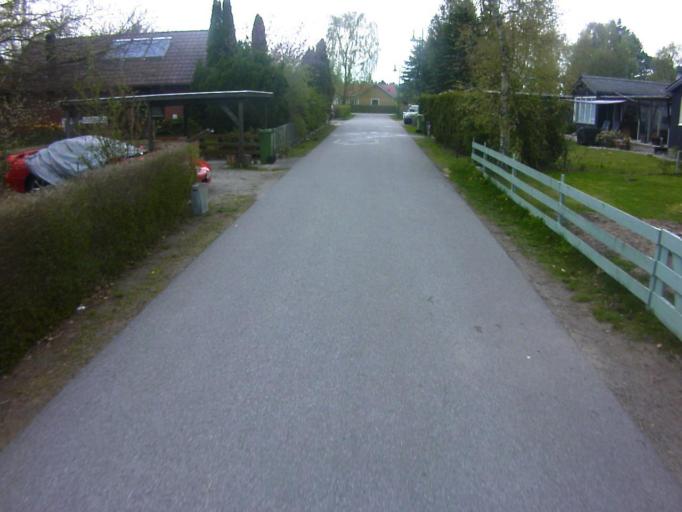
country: SE
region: Skane
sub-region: Kavlinge Kommun
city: Loddekopinge
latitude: 55.7527
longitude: 12.9954
